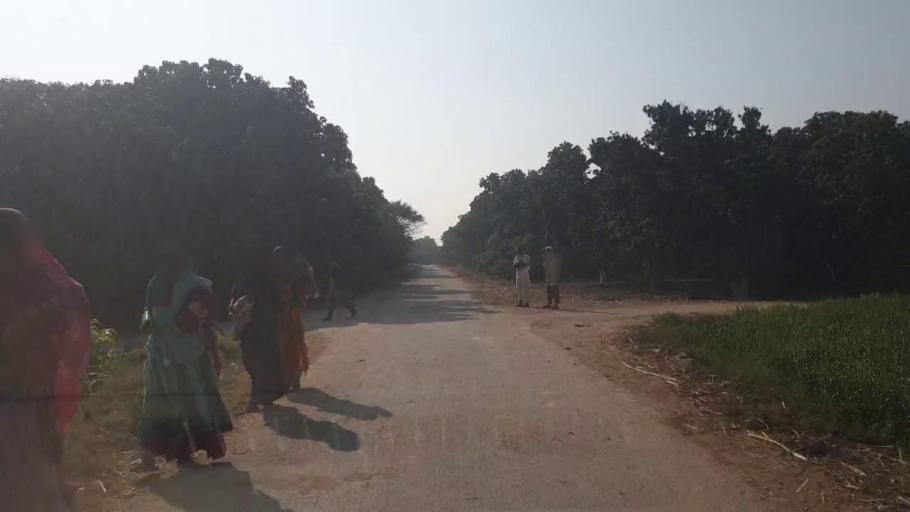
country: PK
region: Sindh
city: Tando Allahyar
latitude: 25.4719
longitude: 68.7623
